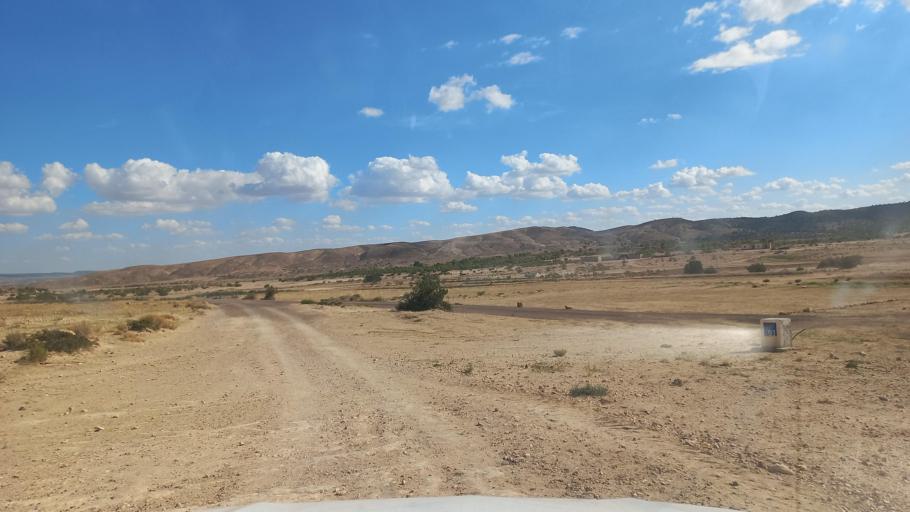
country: TN
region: Al Qasrayn
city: Sbiba
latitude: 35.4050
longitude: 8.9979
